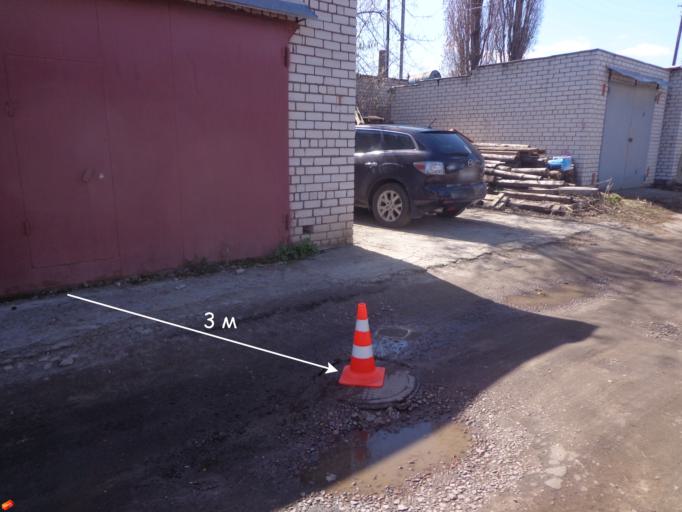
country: RU
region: Voronezj
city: Voronezh
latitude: 51.6967
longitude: 39.2128
